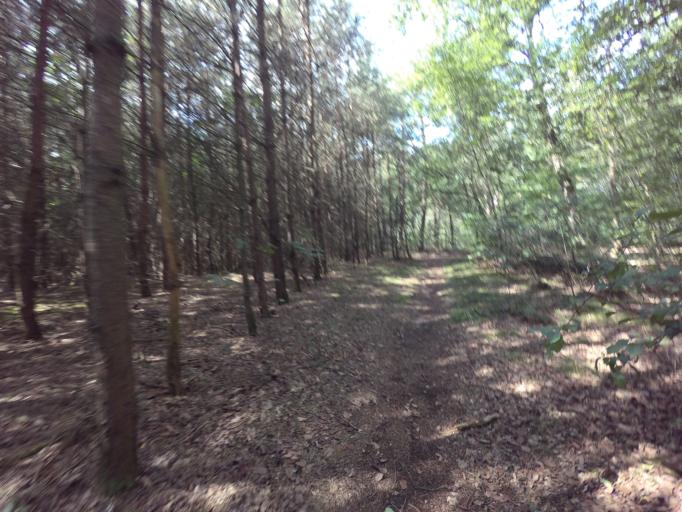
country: NL
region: Overijssel
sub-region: Gemeente Deventer
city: Schalkhaar
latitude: 52.2839
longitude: 6.2384
